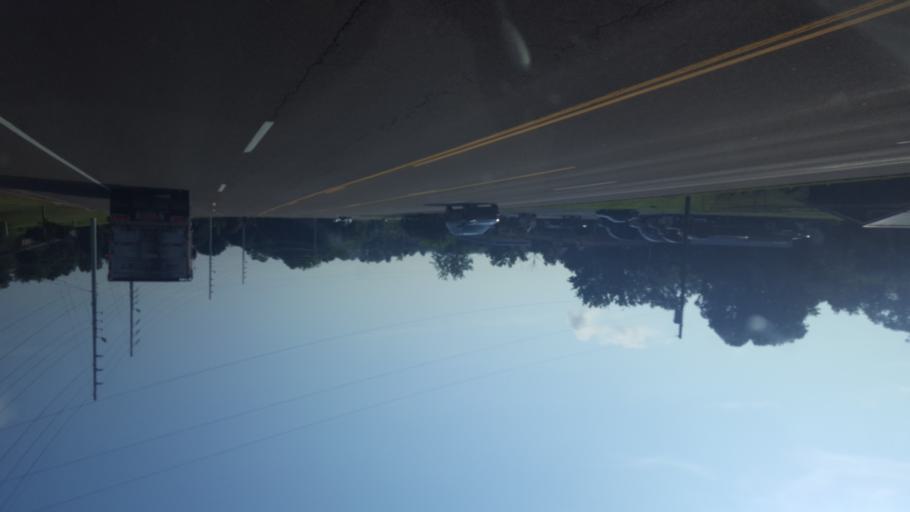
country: US
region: Tennessee
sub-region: Sullivan County
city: Bluff City
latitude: 36.5064
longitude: -82.2710
